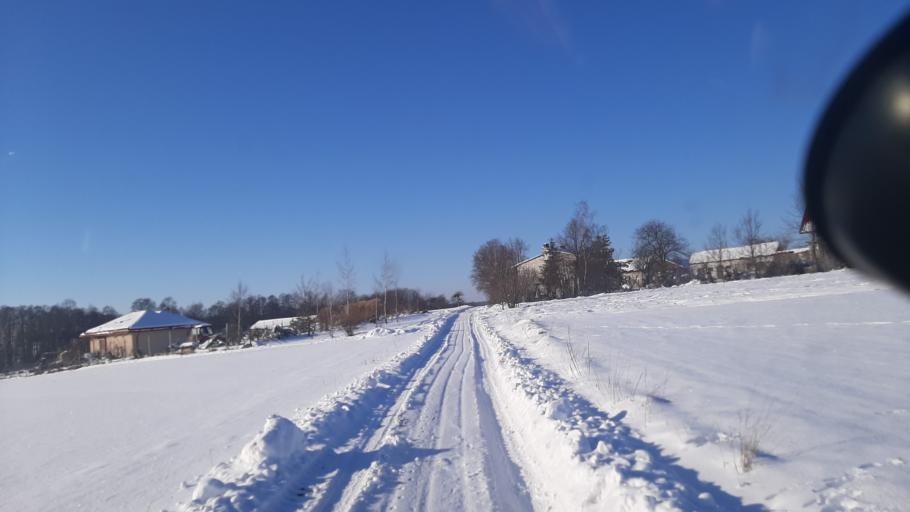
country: PL
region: Lublin Voivodeship
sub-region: Powiat lubelski
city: Jastkow
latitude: 51.3835
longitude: 22.4225
